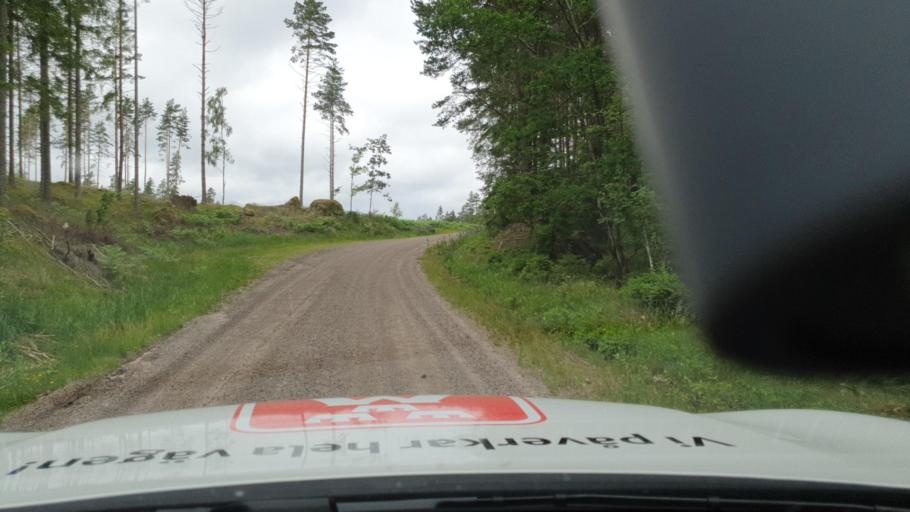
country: SE
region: Vaestra Goetaland
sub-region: Hjo Kommun
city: Hjo
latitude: 58.3972
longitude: 14.3385
